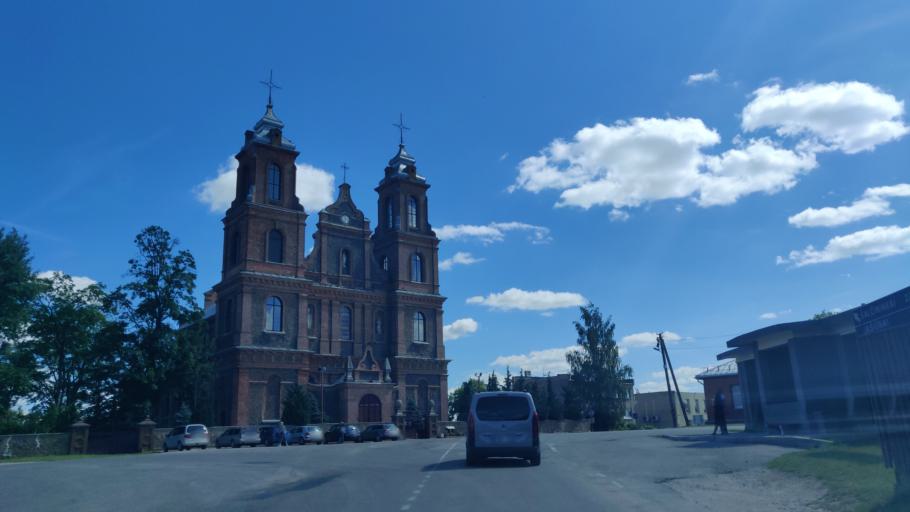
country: LT
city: Salcininkai
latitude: 54.4559
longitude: 25.5073
